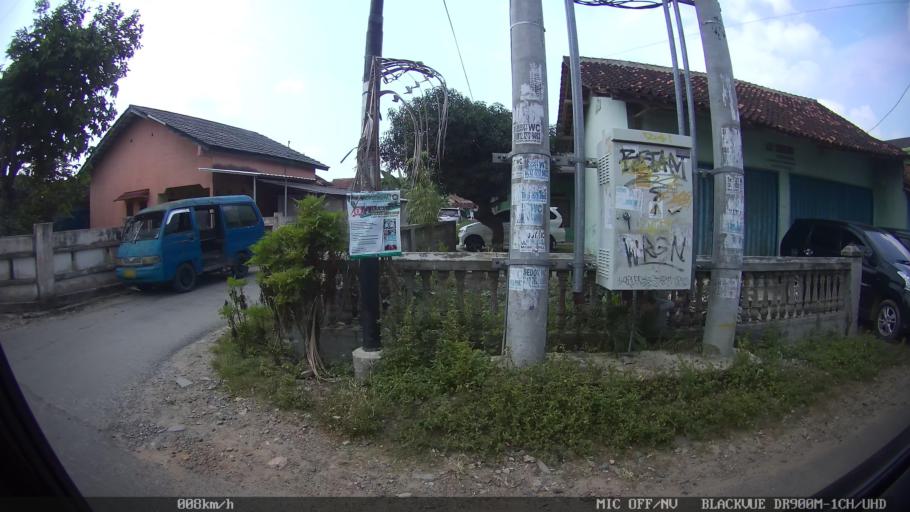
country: ID
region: Lampung
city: Pringsewu
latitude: -5.3596
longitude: 104.9697
